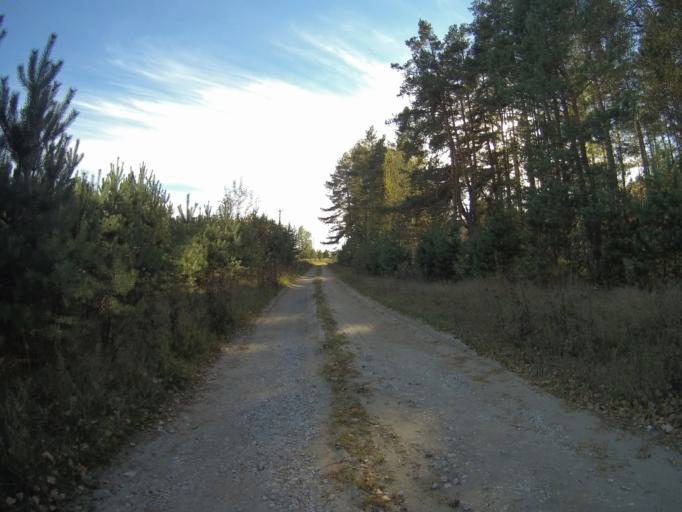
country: RU
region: Vladimir
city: Golovino
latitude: 55.9888
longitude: 40.5216
